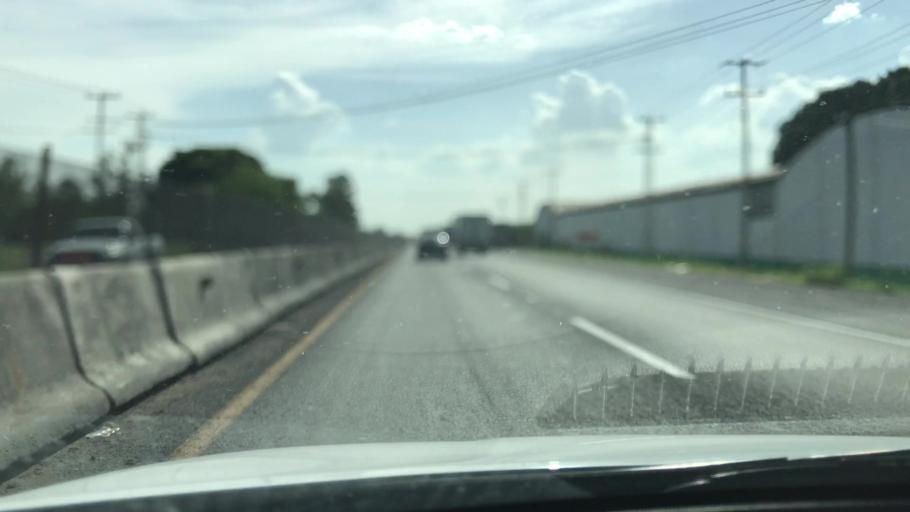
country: MX
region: Guanajuato
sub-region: Villagran
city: El Chinaco (El Pujido)
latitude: 20.5144
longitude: -100.9089
